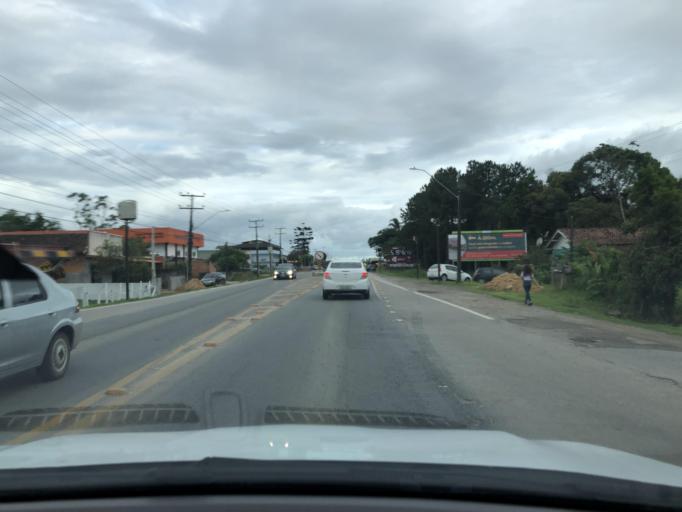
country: BR
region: Santa Catarina
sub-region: Joinville
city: Joinville
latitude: -26.3793
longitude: -48.7219
